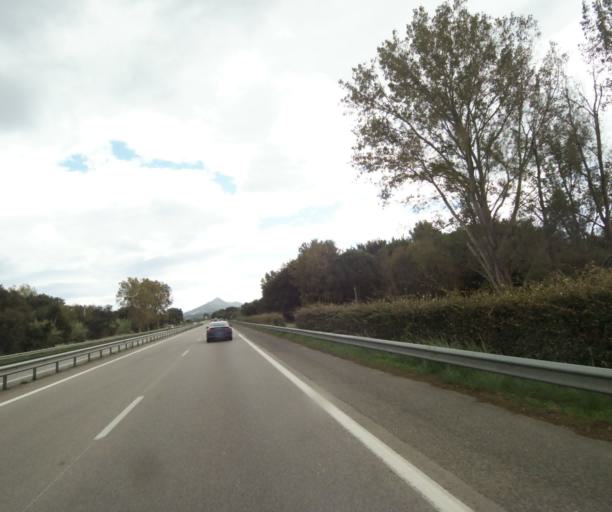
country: FR
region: Languedoc-Roussillon
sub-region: Departement des Pyrenees-Orientales
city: Sant Andreu de Sureda
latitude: 42.5708
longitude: 2.9986
